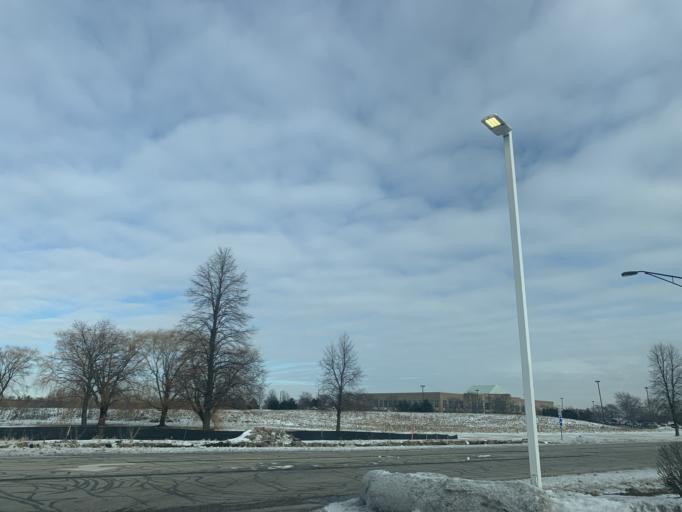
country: US
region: Illinois
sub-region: Will County
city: Romeoville
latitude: 41.6587
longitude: -88.1239
